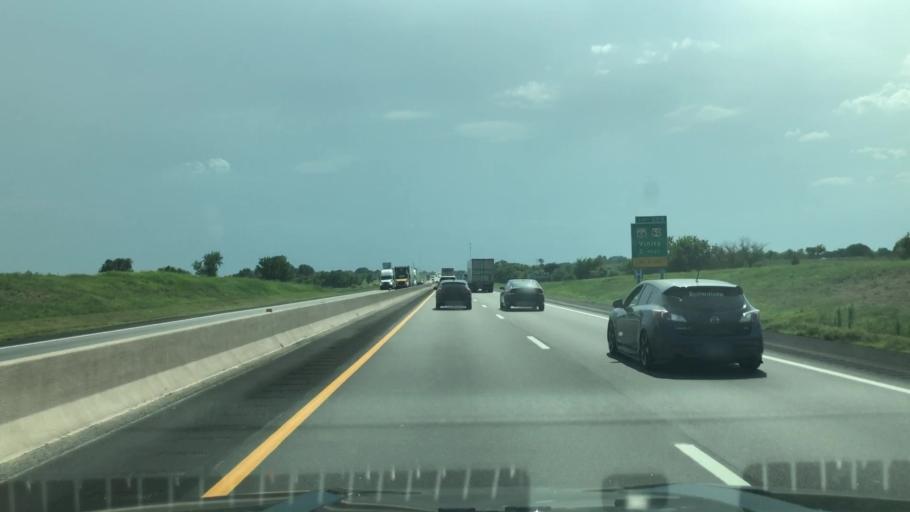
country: US
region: Oklahoma
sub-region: Craig County
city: Vinita
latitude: 36.6529
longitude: -95.1059
